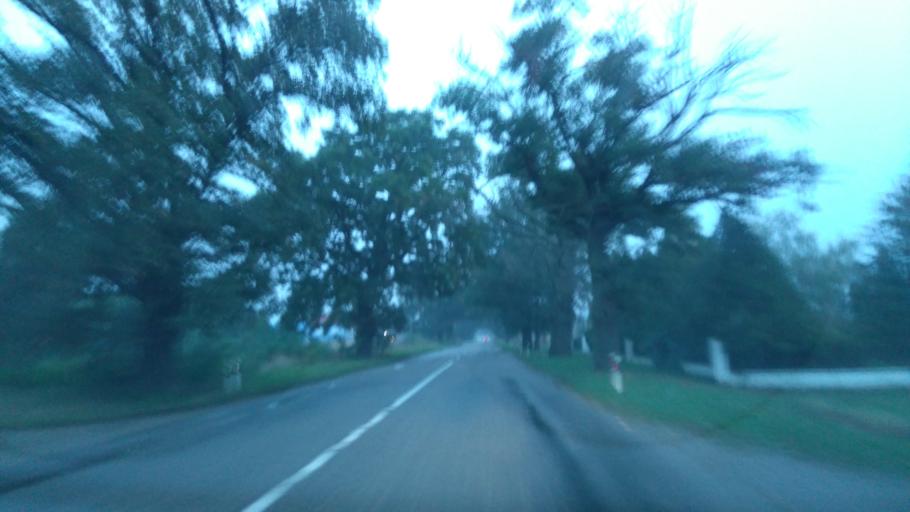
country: RS
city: Backo Petrovo Selo
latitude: 45.6912
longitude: 20.0785
